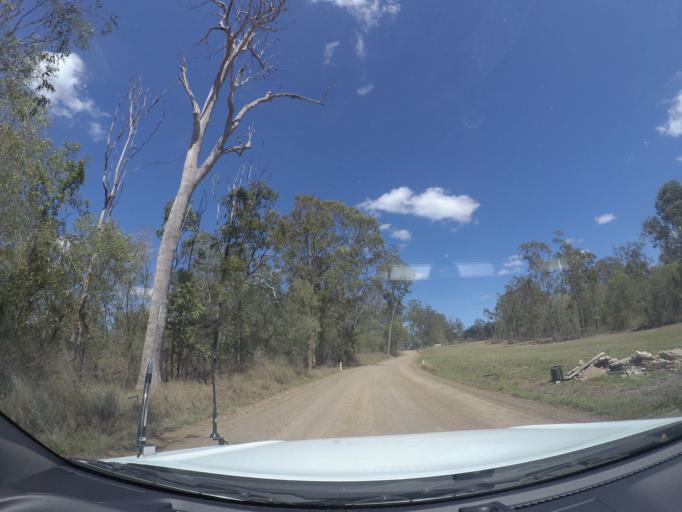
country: AU
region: Queensland
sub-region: Logan
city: Cedar Vale
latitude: -27.8384
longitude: 152.9318
